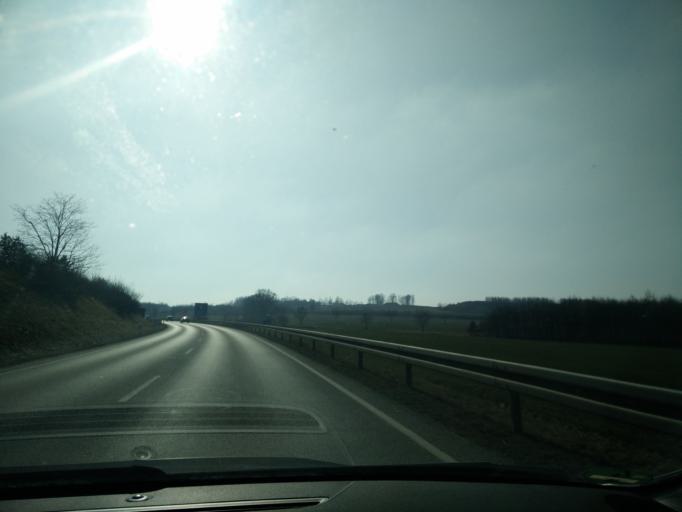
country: DE
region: Saxony
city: Hartmannsdorf
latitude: 50.8870
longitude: 12.7835
